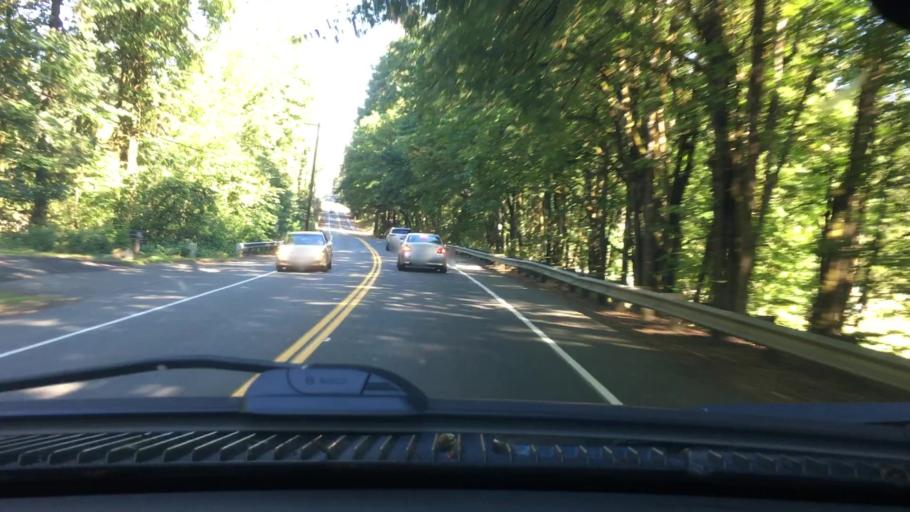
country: US
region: Washington
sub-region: King County
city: Lake Morton-Berrydale
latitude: 47.3362
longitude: -122.1237
